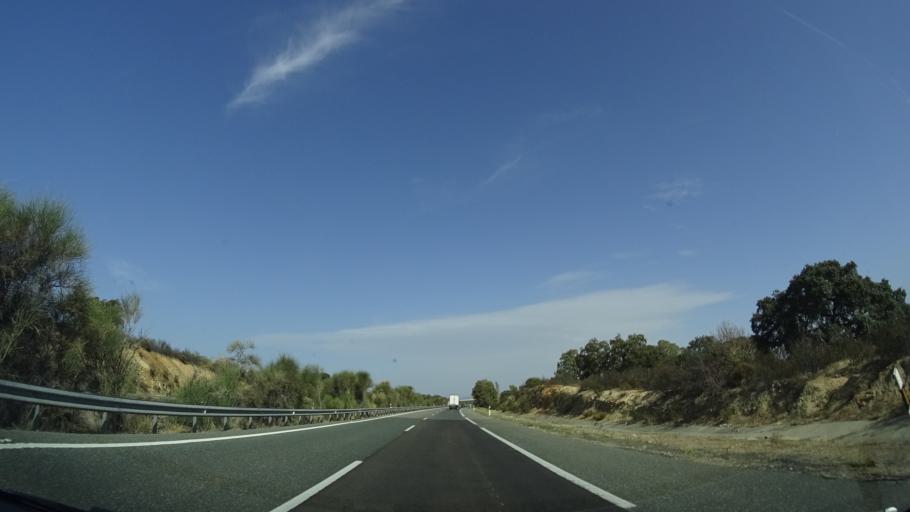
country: ES
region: Andalusia
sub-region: Provincia de Huelva
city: Santa Olalla del Cala
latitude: 37.8372
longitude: -6.2201
